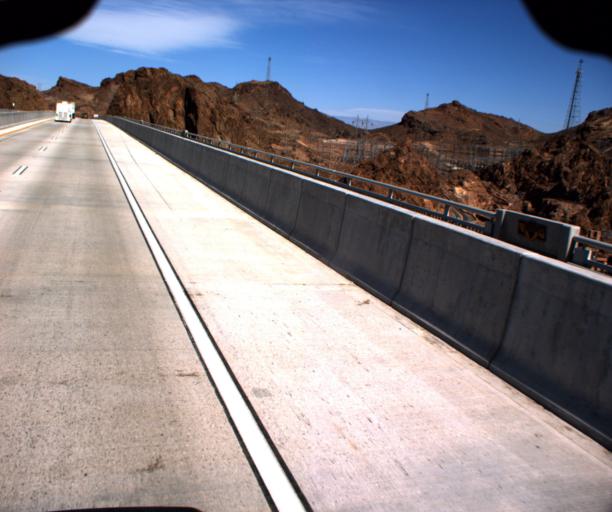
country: US
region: Nevada
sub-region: Clark County
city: Boulder City
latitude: 36.0119
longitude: -114.7382
